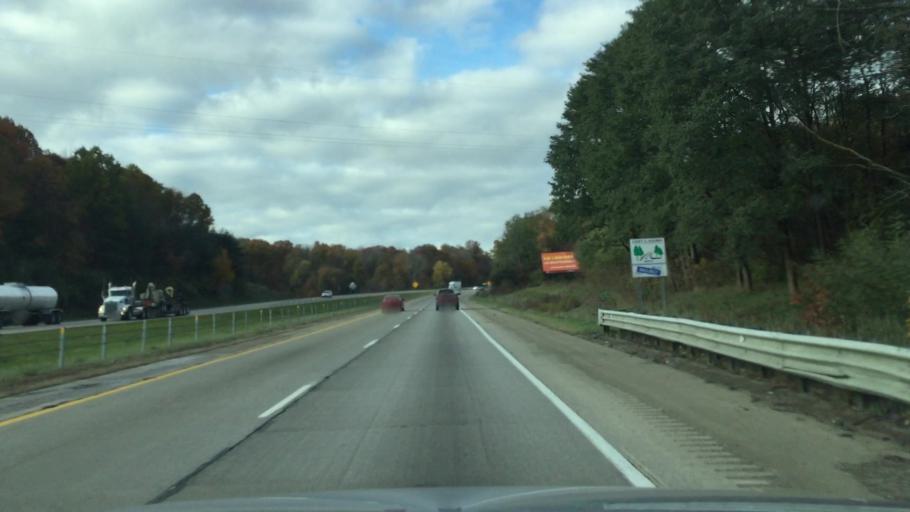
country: US
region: Michigan
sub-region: Calhoun County
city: Brownlee Park
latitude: 42.2892
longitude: -85.1150
